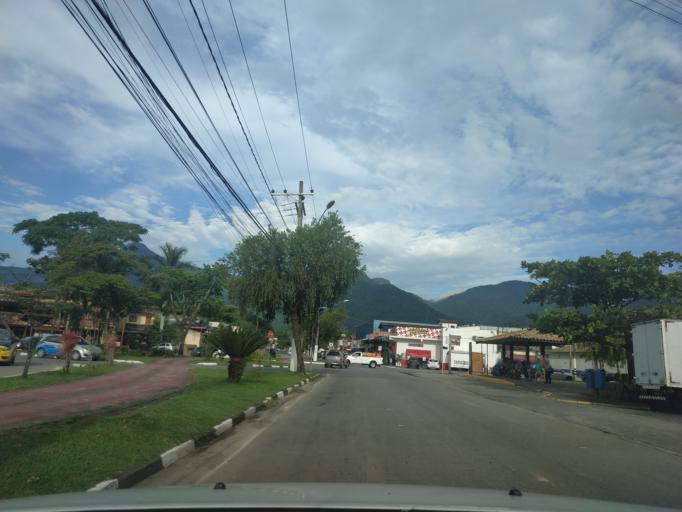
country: BR
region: Sao Paulo
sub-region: Ilhabela
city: Ilhabela
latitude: -23.8224
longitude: -45.3756
